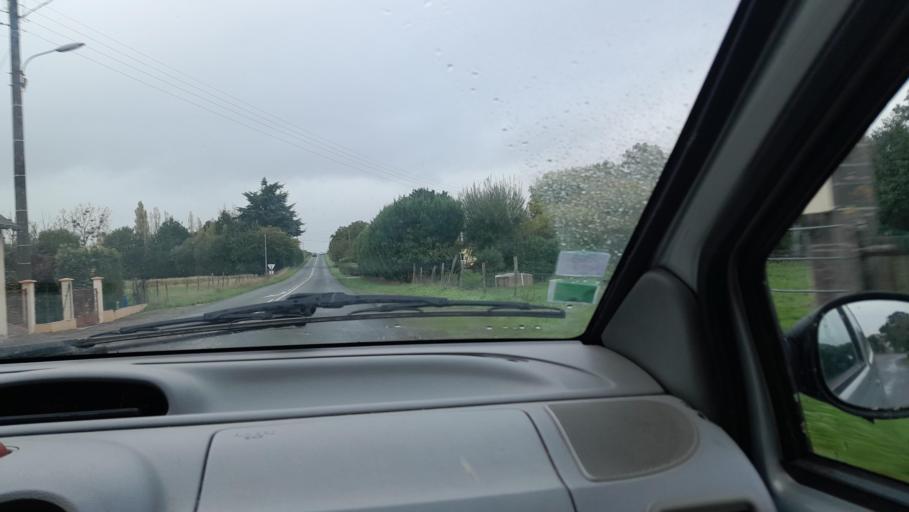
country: FR
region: Pays de la Loire
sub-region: Departement de la Mayenne
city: Congrier
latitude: 47.8470
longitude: -1.1361
